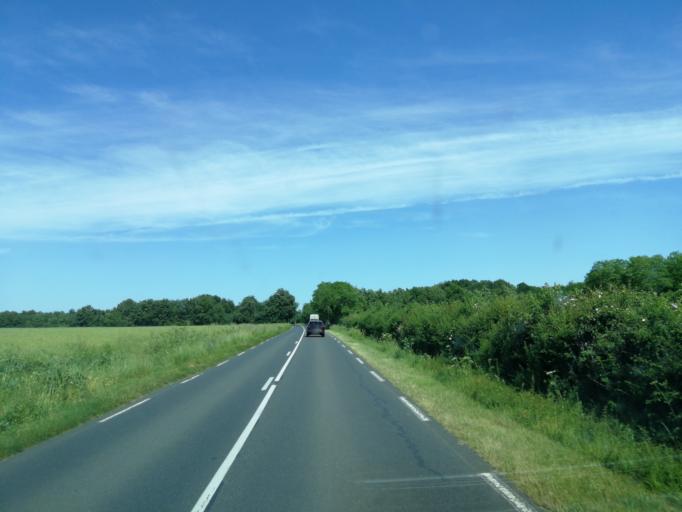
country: FR
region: Poitou-Charentes
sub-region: Departement des Deux-Sevres
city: Saint-Leger-de-Montbrun
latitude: 46.9719
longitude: -0.1198
